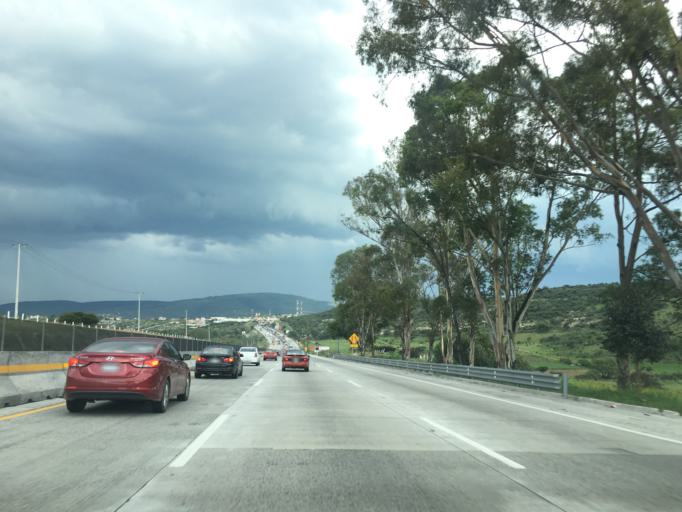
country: MX
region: Hidalgo
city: Tepeji de Ocampo
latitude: 19.9164
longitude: -99.3655
